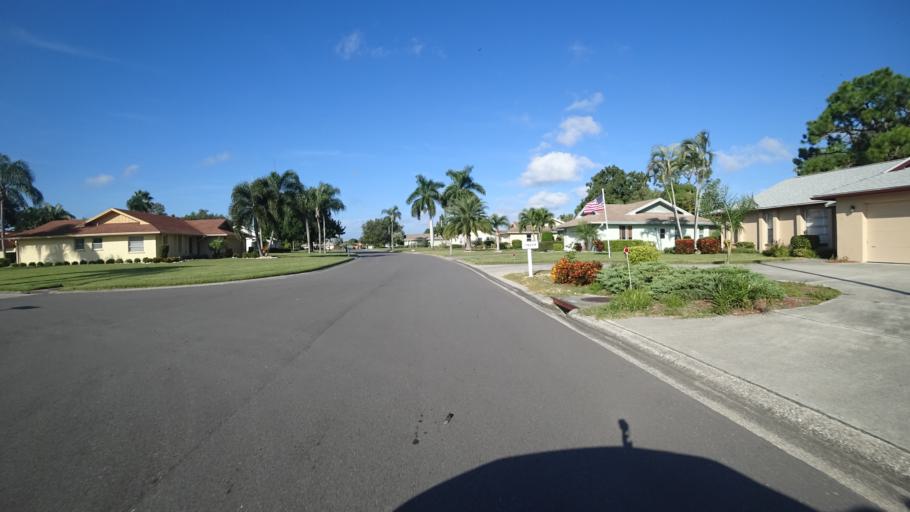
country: US
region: Florida
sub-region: Manatee County
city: West Bradenton
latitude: 27.4900
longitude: -82.6188
